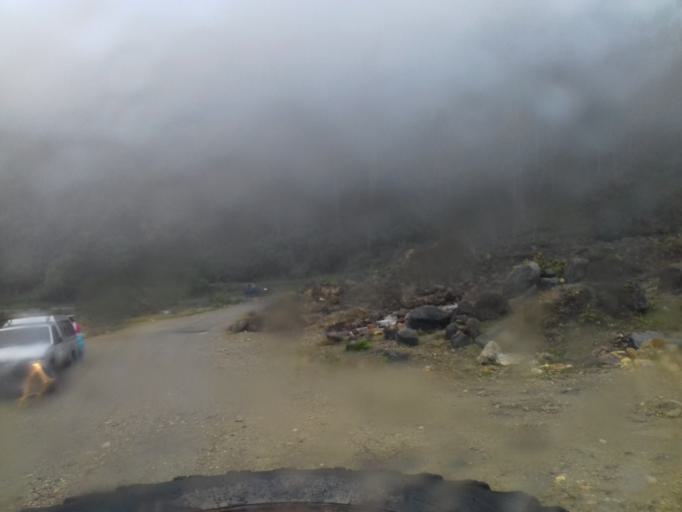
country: CO
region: Tolima
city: Murillo
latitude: 4.8914
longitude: -75.2618
